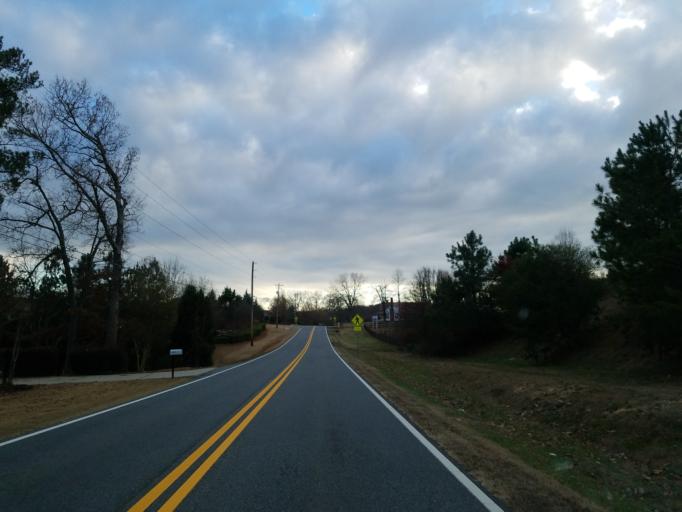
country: US
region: Georgia
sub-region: Forsyth County
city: Cumming
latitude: 34.3008
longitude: -84.0814
